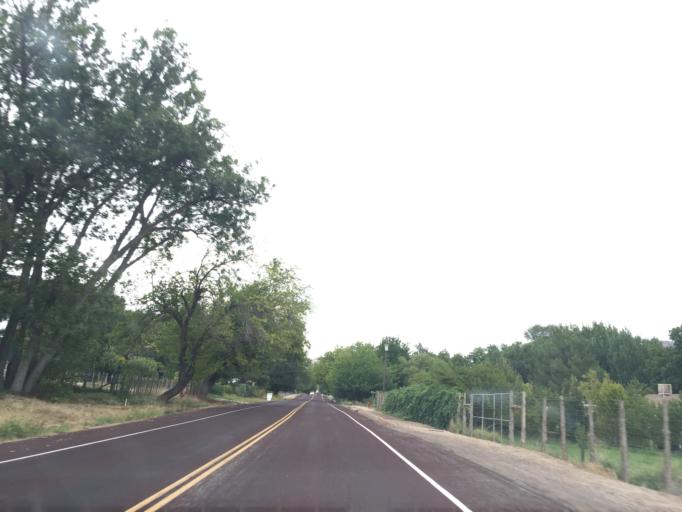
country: US
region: Utah
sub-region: Washington County
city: Hildale
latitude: 37.1609
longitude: -113.0496
